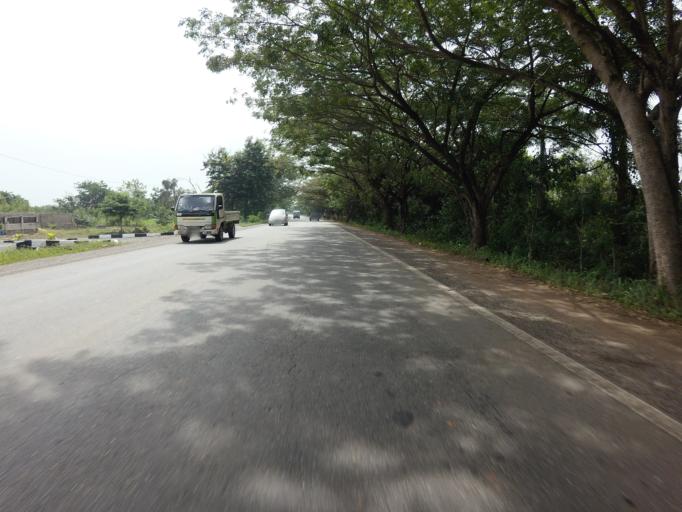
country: GH
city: Akropong
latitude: 6.1255
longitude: 0.0479
